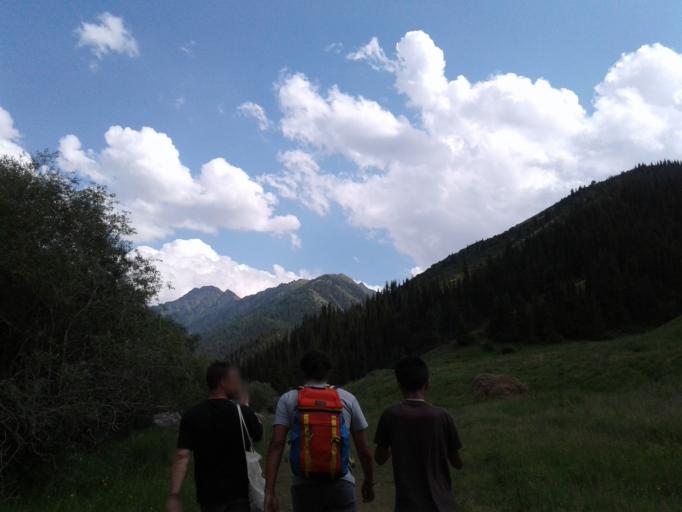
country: KG
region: Naryn
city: Naryn
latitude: 41.4577
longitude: 76.4527
